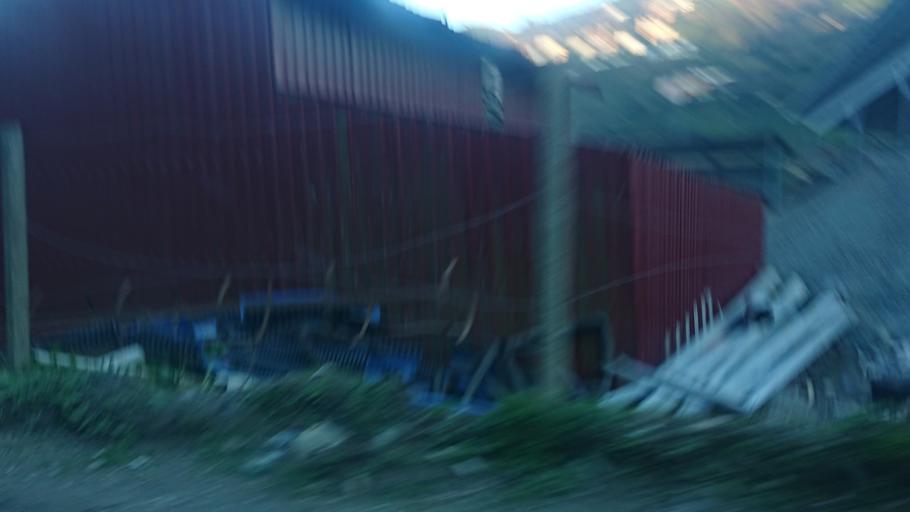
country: TR
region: Rize
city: Gundogdu
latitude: 41.0251
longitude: 40.5777
